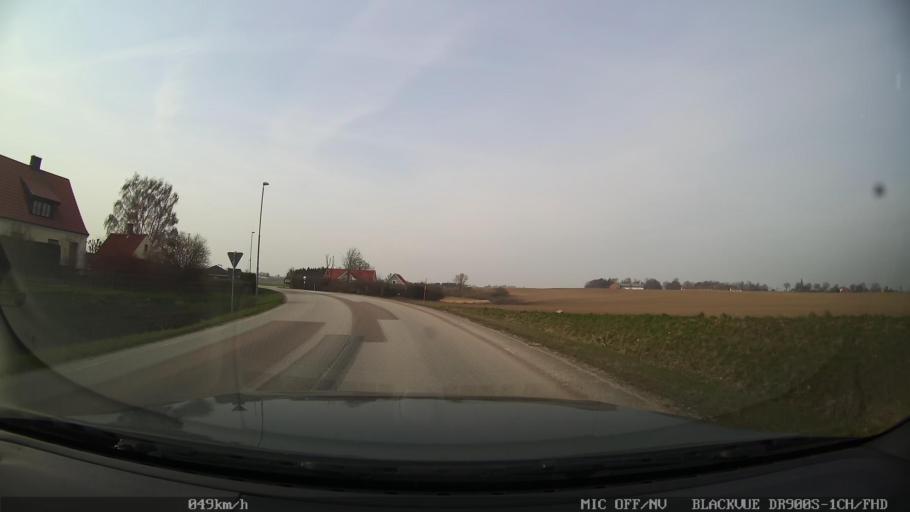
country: SE
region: Skane
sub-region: Ystads Kommun
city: Ystad
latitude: 55.4450
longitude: 13.8355
